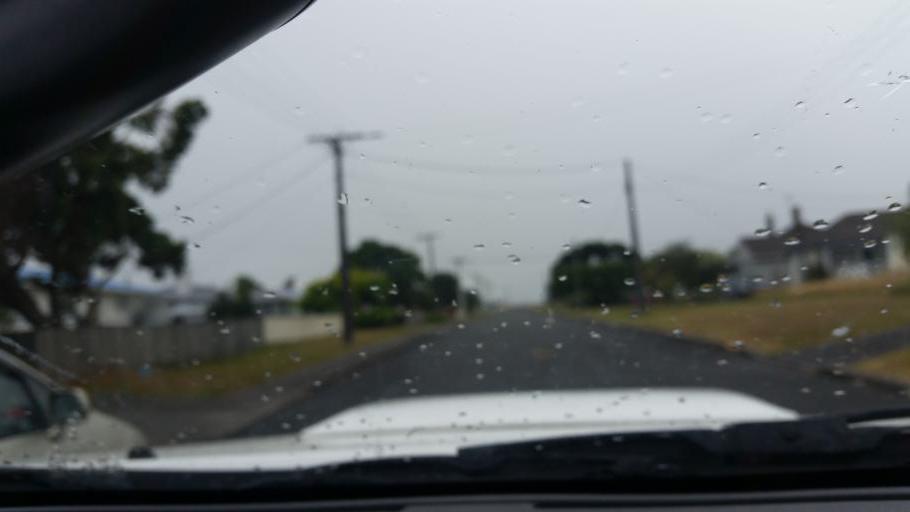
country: NZ
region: Northland
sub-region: Kaipara District
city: Dargaville
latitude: -35.9351
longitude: 173.8704
